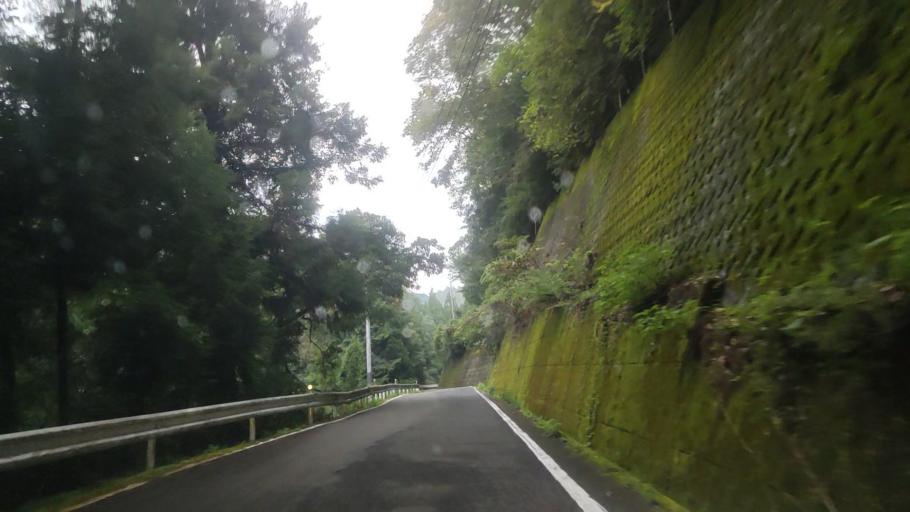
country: JP
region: Wakayama
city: Hashimoto
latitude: 34.2866
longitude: 135.6261
